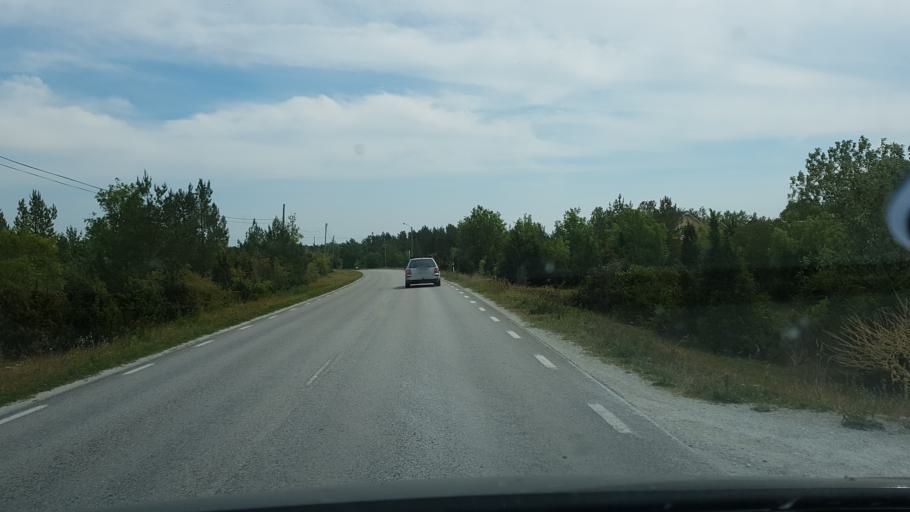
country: SE
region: Gotland
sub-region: Gotland
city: Slite
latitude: 57.7330
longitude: 18.7404
